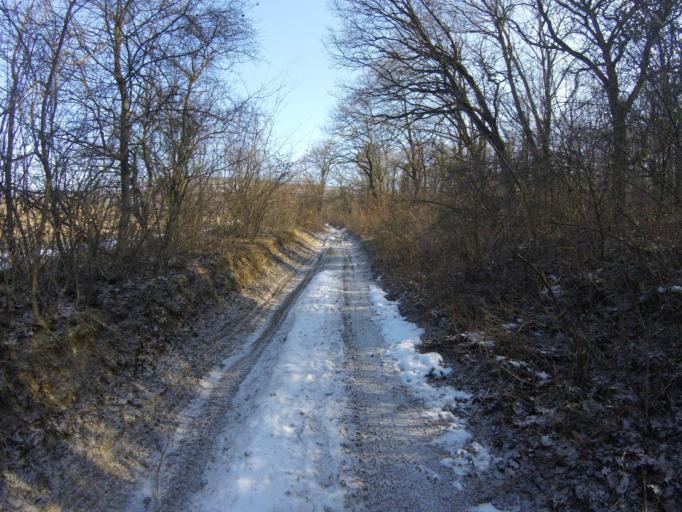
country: HU
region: Komarom-Esztergom
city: Piliscsev
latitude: 47.6740
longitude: 18.8324
